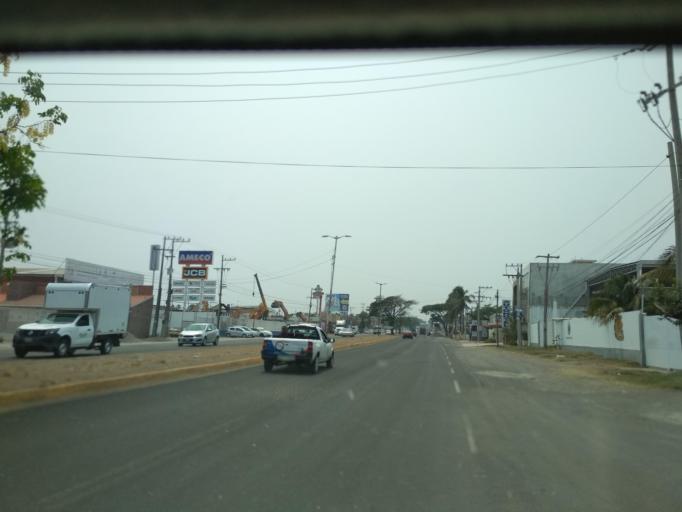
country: MX
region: Veracruz
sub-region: Veracruz
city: Las Amapolas
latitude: 19.1620
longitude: -96.2058
